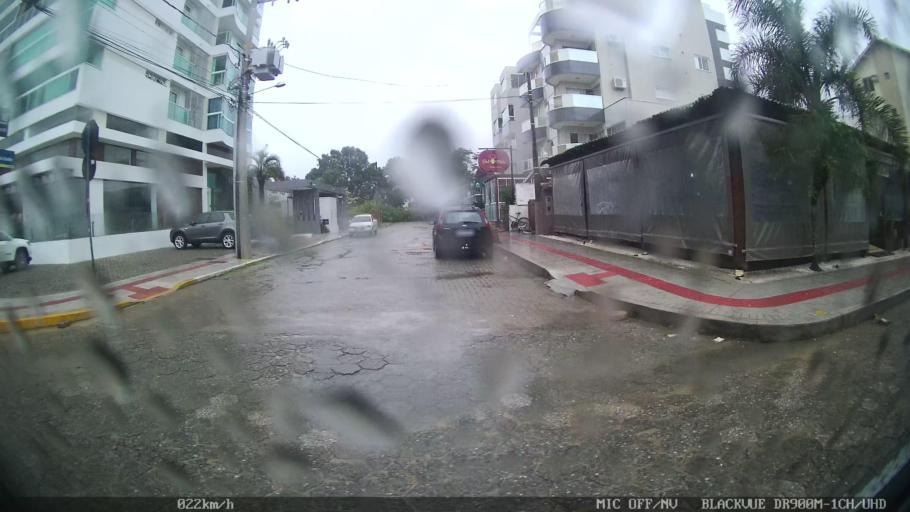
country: BR
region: Santa Catarina
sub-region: Balneario Camboriu
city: Balneario Camboriu
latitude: -26.9557
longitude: -48.6317
